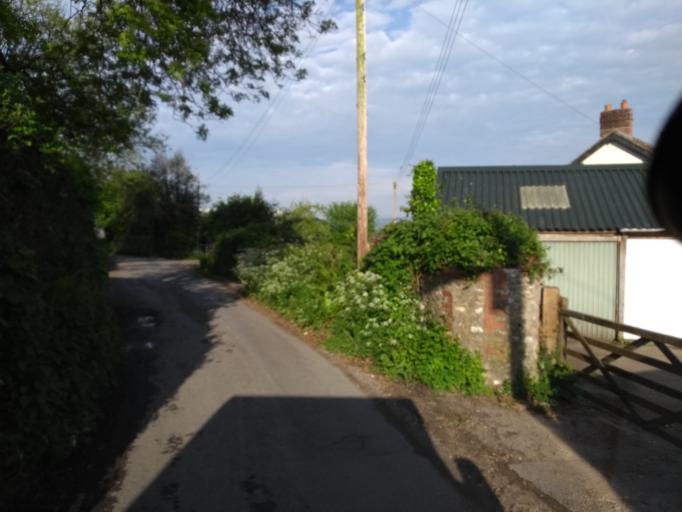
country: GB
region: England
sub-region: Devon
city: Axminster
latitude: 50.8002
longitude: -2.9389
